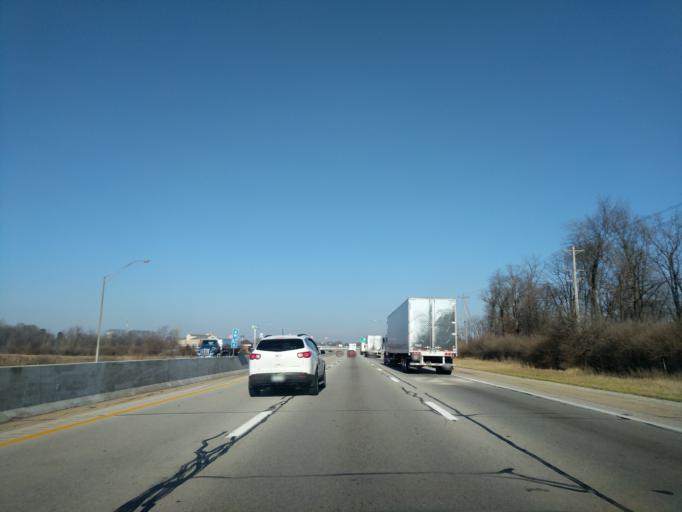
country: US
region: Ohio
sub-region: Miami County
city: Tipp City
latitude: 39.9556
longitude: -84.1893
